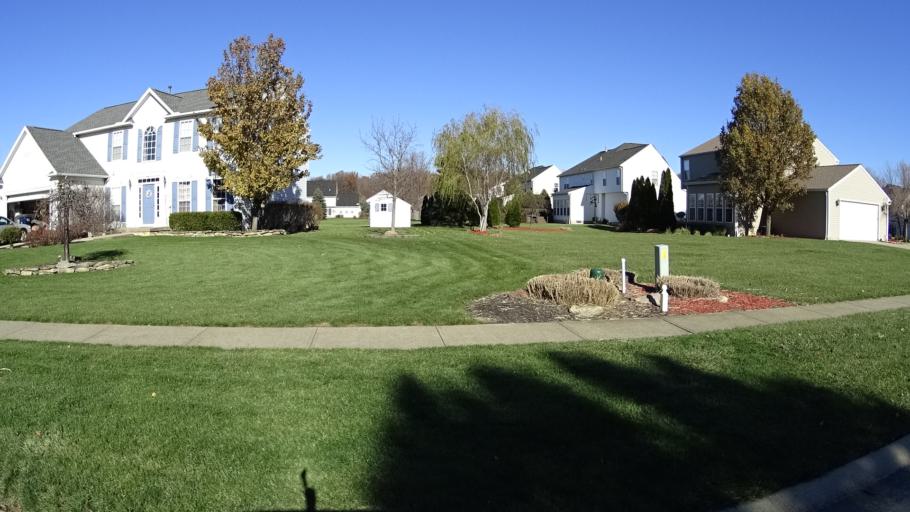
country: US
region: Ohio
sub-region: Lorain County
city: Avon
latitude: 41.4203
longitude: -82.0554
